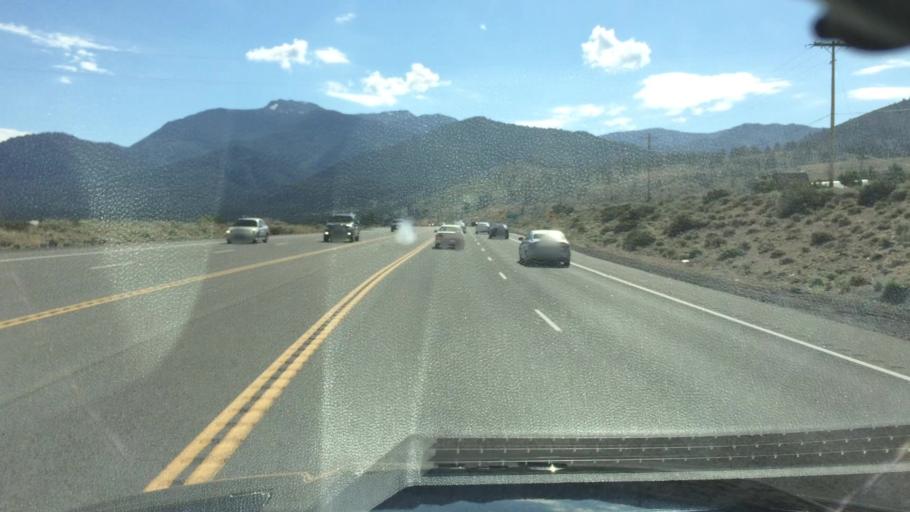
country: US
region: Nevada
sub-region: Washoe County
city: Reno
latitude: 39.3795
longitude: -119.8258
